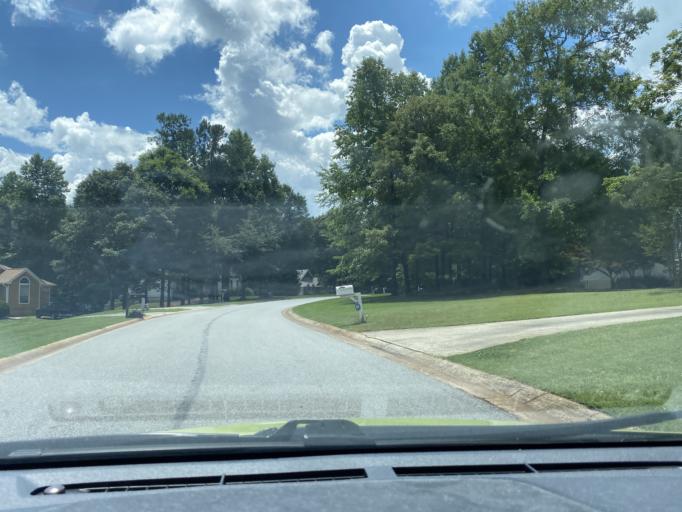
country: US
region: Georgia
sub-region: Fulton County
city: Palmetto
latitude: 33.4333
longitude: -84.6838
